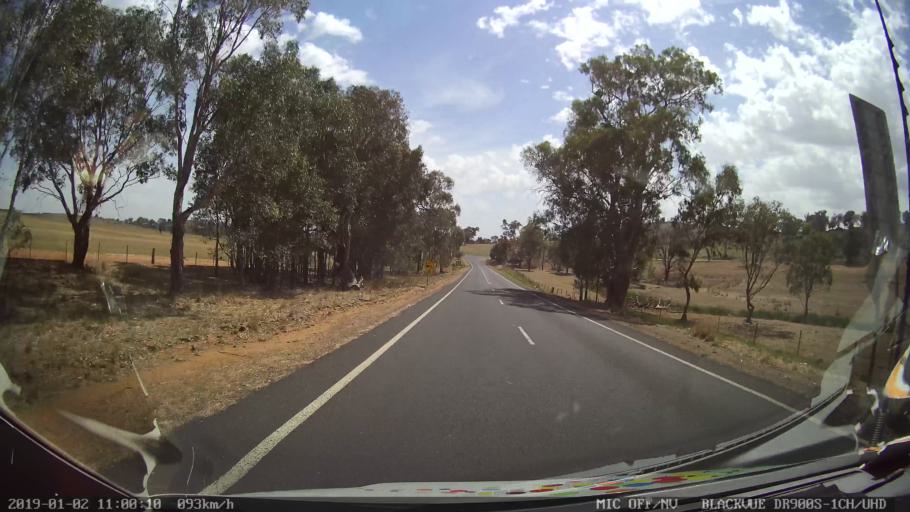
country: AU
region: New South Wales
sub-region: Cootamundra
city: Cootamundra
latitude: -34.6075
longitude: 148.3125
